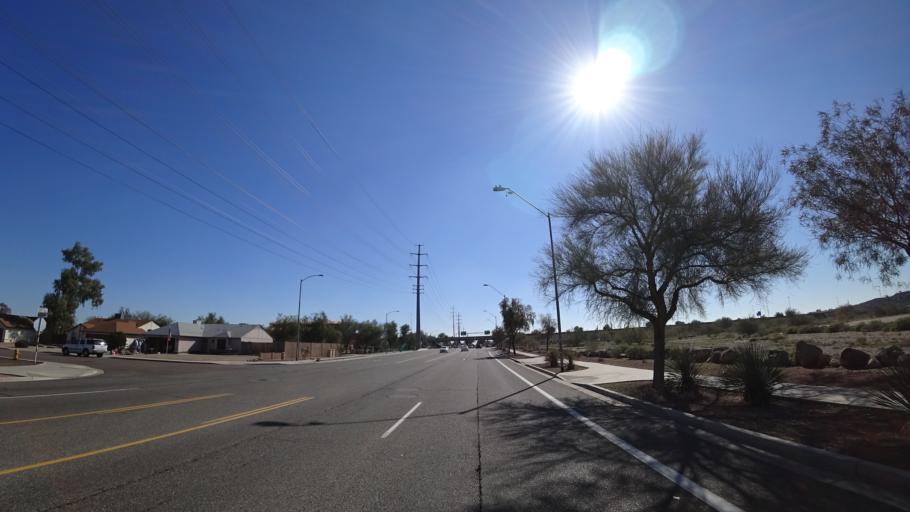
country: US
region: Arizona
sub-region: Maricopa County
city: Peoria
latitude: 33.6719
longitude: -112.1348
